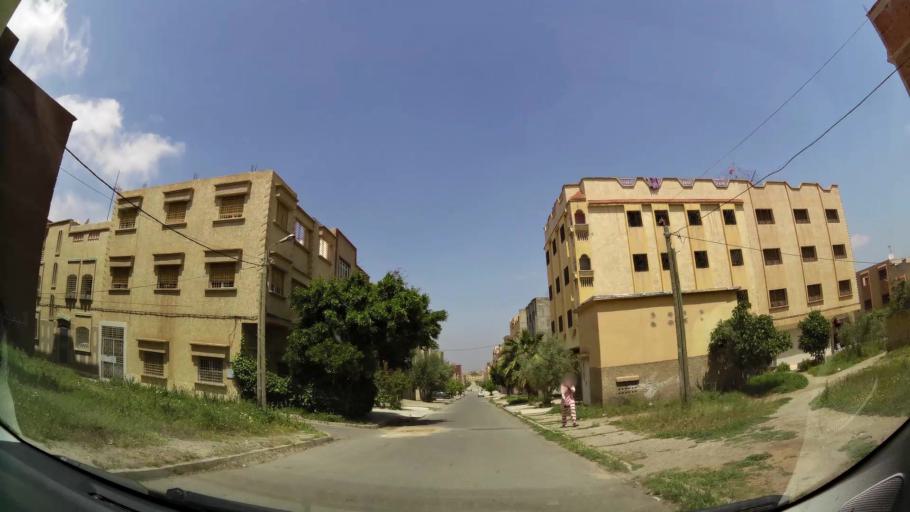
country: MA
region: Oriental
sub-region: Oujda-Angad
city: Oujda
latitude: 34.6863
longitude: -1.8827
